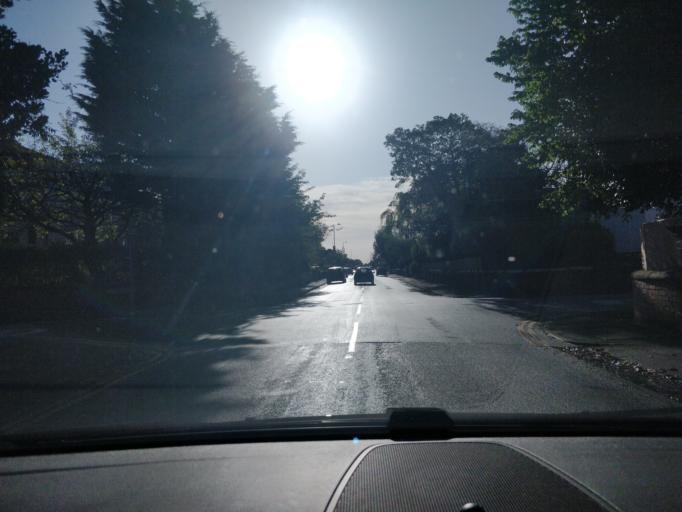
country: GB
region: England
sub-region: Sefton
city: Southport
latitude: 53.6408
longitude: -3.0083
